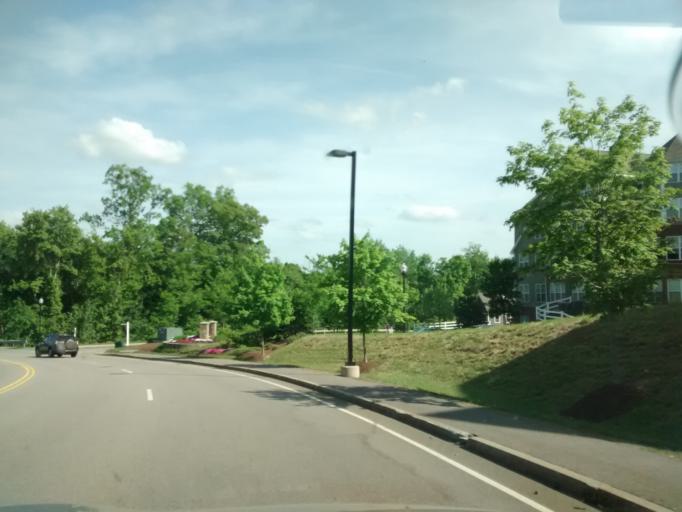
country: US
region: Massachusetts
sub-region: Worcester County
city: Shrewsbury
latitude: 42.2870
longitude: -71.6731
